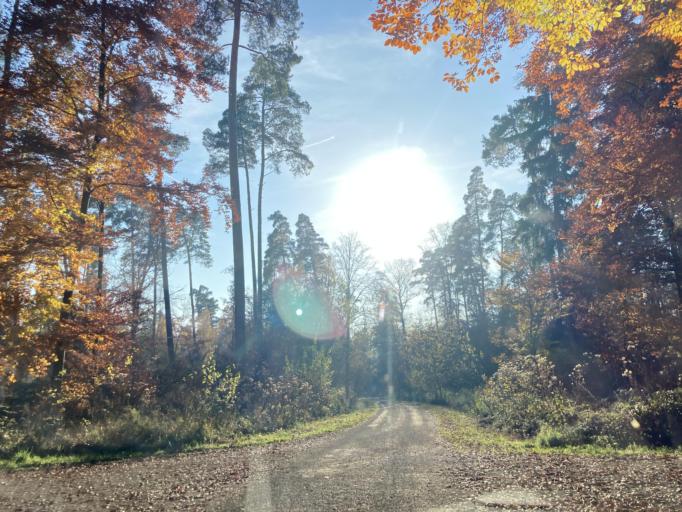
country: DE
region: Baden-Wuerttemberg
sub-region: Tuebingen Region
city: Tuebingen
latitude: 48.5497
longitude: 8.9997
